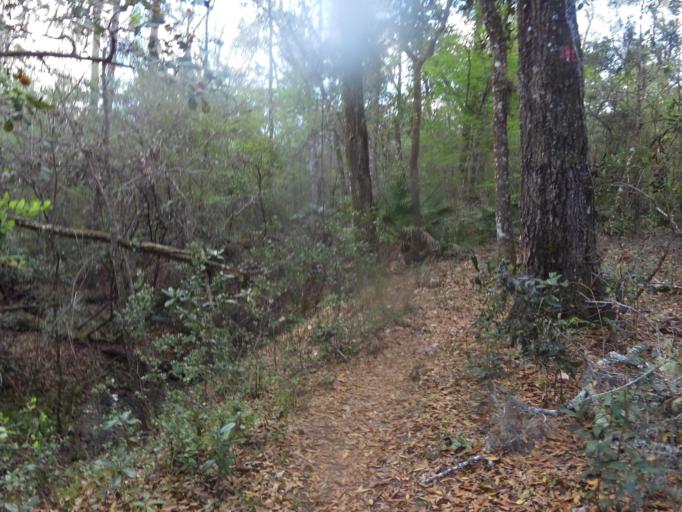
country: US
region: Florida
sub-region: Putnam County
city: Interlachen
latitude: 29.7639
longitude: -81.8275
